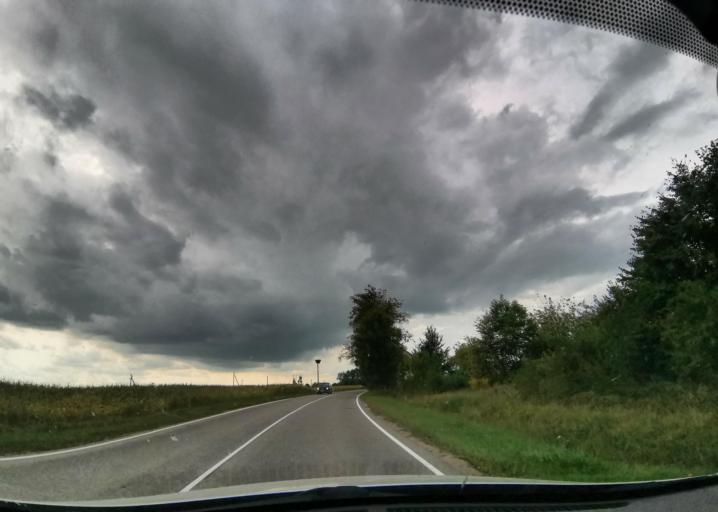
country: RU
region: Kaliningrad
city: Gusev
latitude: 54.6025
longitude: 22.1131
